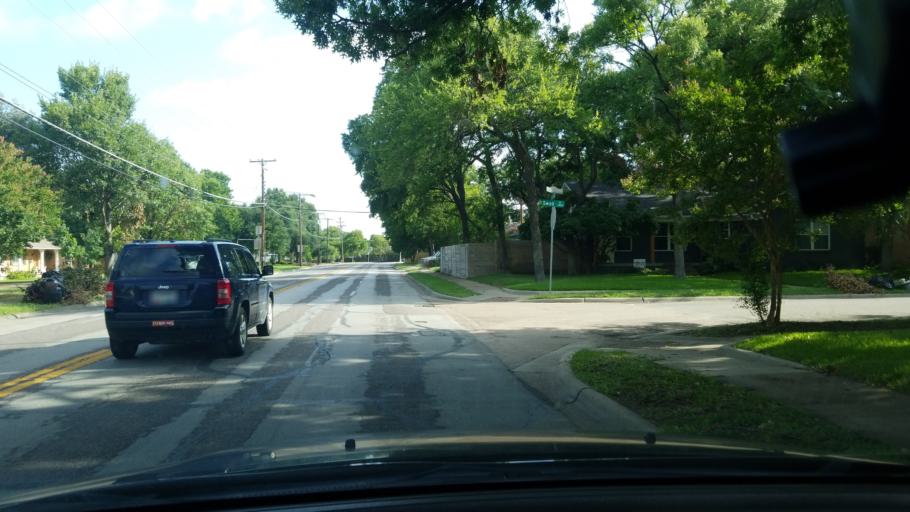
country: US
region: Texas
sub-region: Dallas County
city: Mesquite
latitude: 32.8198
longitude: -96.6844
